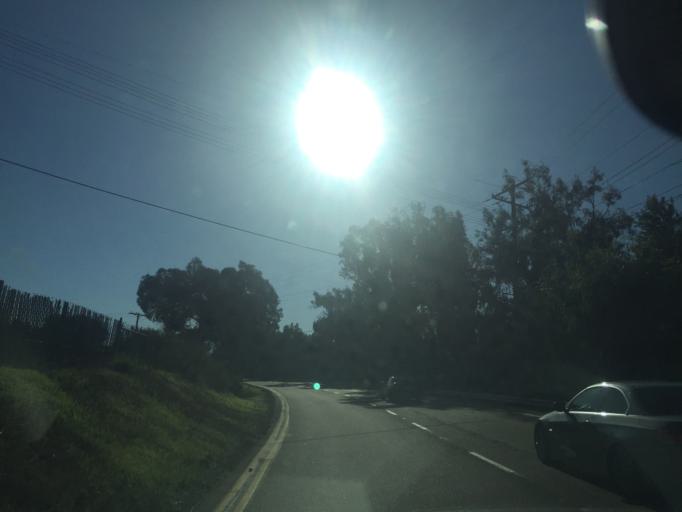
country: US
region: California
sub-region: San Diego County
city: San Diego
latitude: 32.7591
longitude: -117.1011
